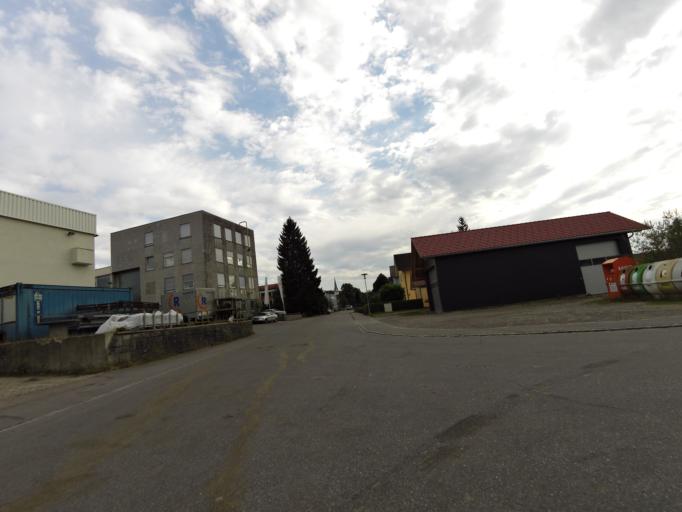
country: DE
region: Bavaria
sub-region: Swabia
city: Weiler-Simmerberg
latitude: 47.5864
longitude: 9.9184
